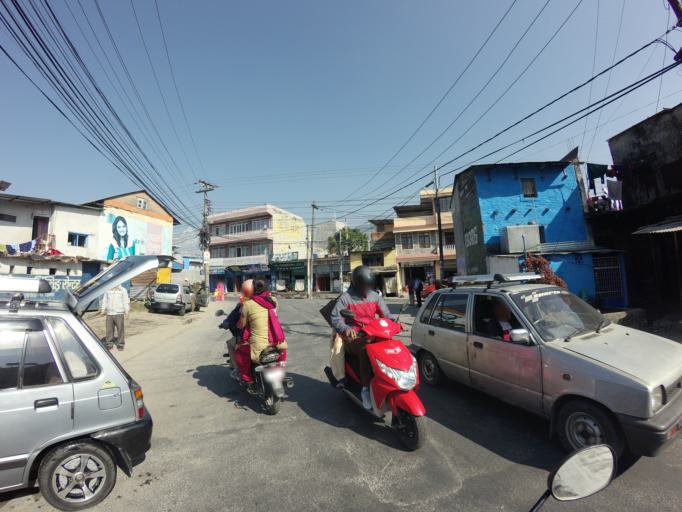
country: NP
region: Western Region
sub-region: Gandaki Zone
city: Pokhara
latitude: 28.2199
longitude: 83.9976
